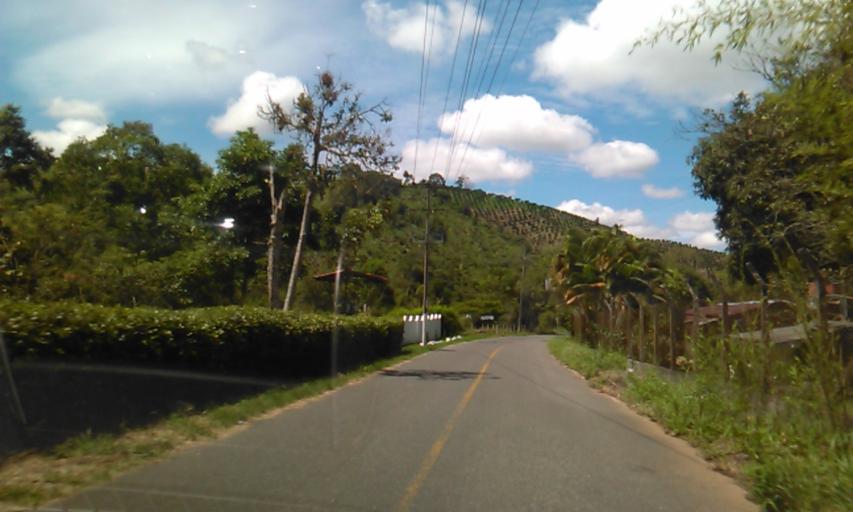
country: CO
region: Quindio
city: Cordoba
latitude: 4.4010
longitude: -75.7198
